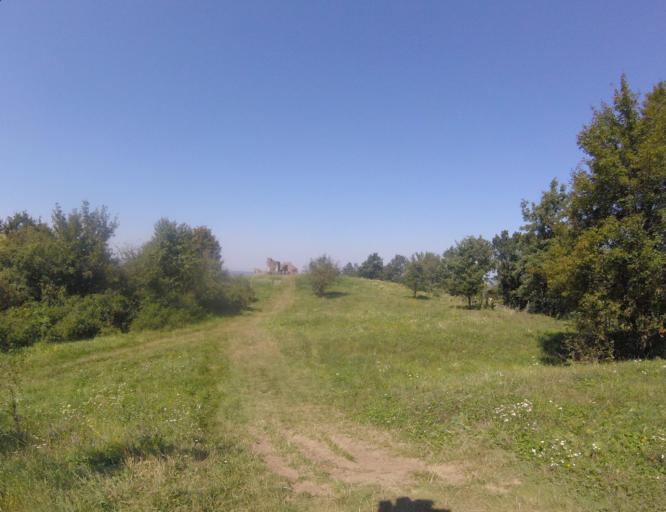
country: HU
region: Nograd
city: Rimoc
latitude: 47.9967
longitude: 19.5850
